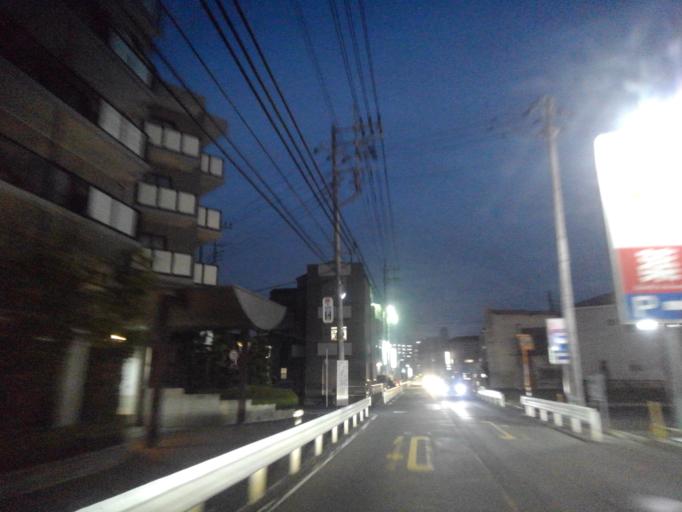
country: JP
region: Saitama
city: Tokorozawa
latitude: 35.8115
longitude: 139.4490
